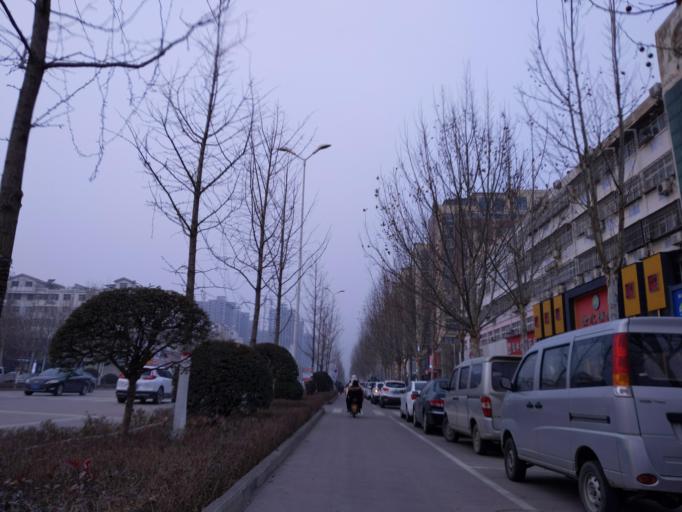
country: CN
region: Henan Sheng
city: Puyang
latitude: 35.7820
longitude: 115.0267
